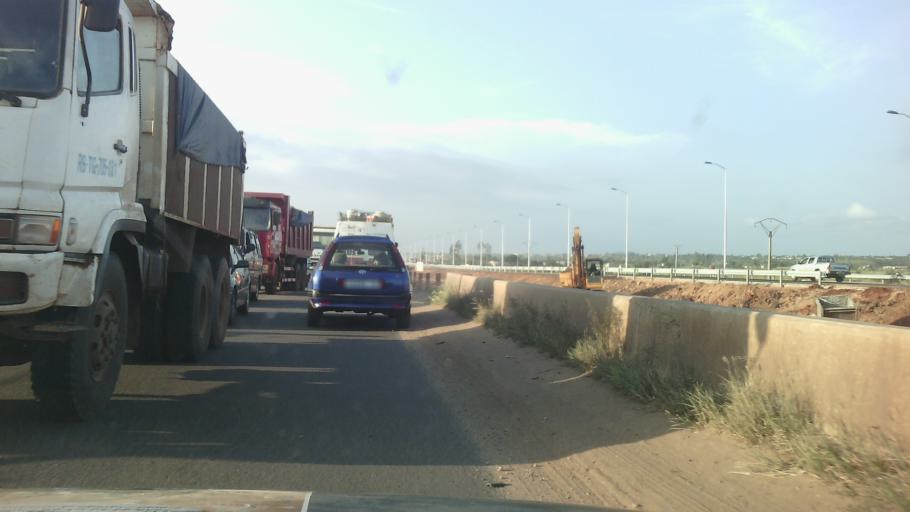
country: TG
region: Maritime
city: Tsevie
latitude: 6.2884
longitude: 1.2127
